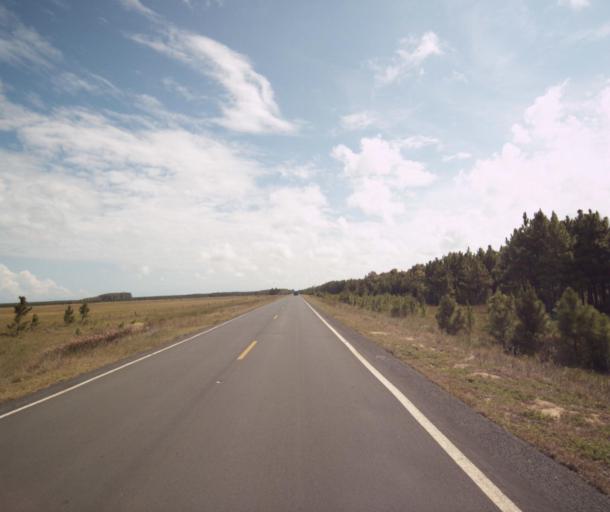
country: BR
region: Rio Grande do Sul
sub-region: Sao Lourenco Do Sul
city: Sao Lourenco do Sul
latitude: -31.4513
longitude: -51.2136
